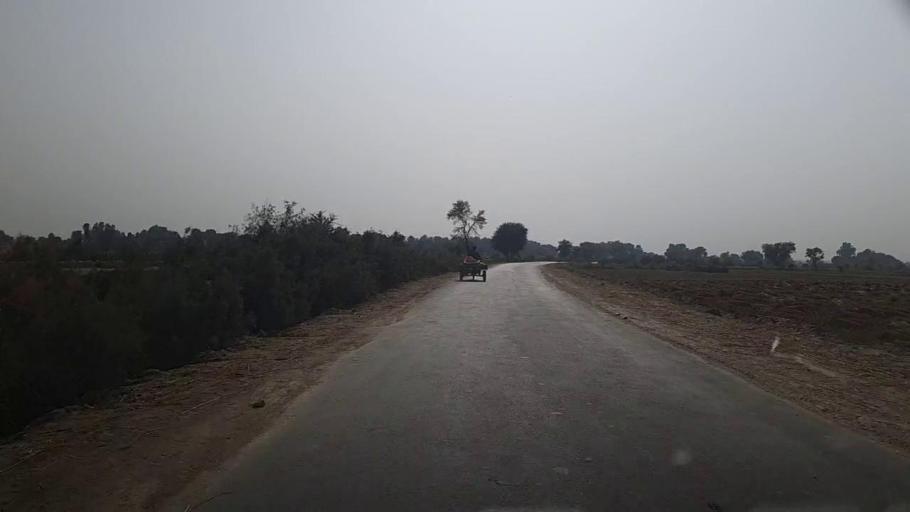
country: PK
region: Sindh
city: Kashmor
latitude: 28.4124
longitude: 69.5660
